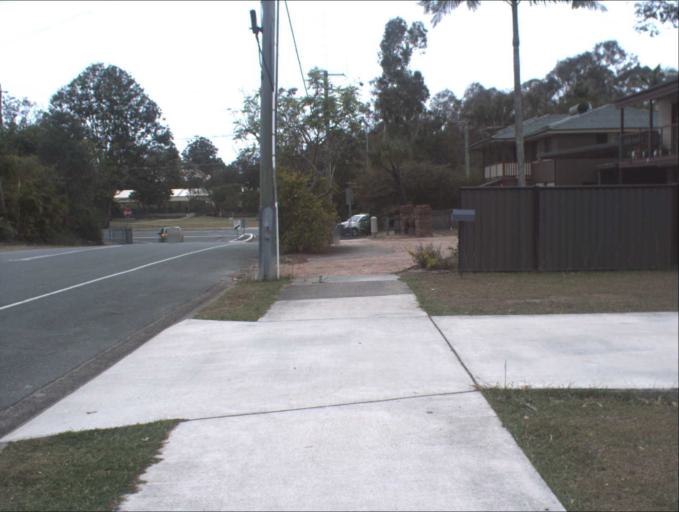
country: AU
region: Queensland
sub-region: Logan
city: Beenleigh
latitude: -27.7110
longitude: 153.1939
